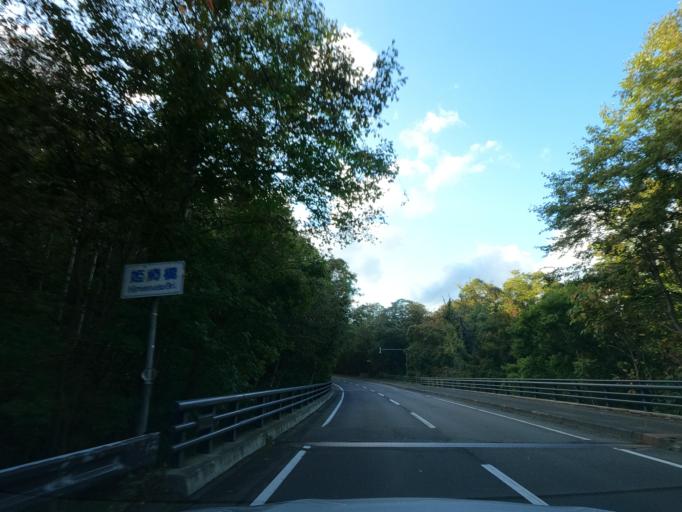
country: JP
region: Hokkaido
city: Shiraoi
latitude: 42.7370
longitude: 141.3599
